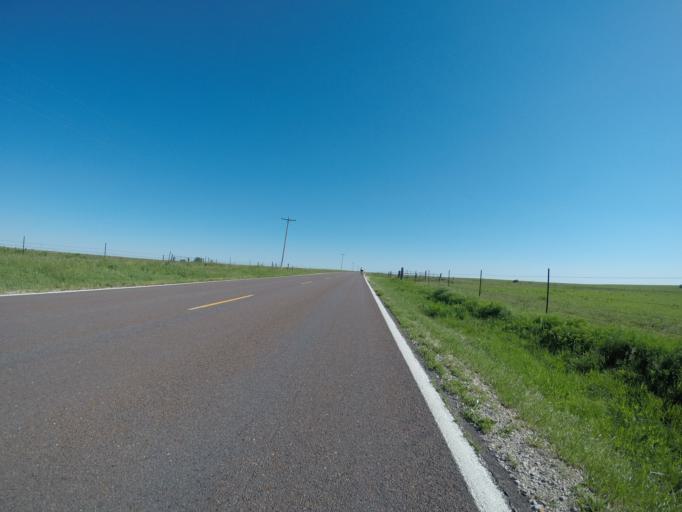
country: US
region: Kansas
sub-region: Osage County
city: Osage City
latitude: 38.6805
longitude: -96.0974
